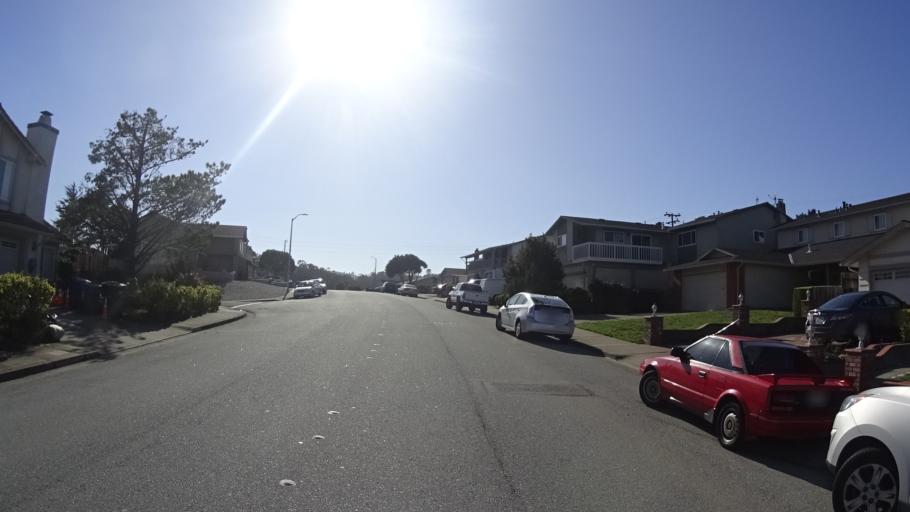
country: US
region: California
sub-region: San Mateo County
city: San Bruno
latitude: 37.6380
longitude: -122.4465
